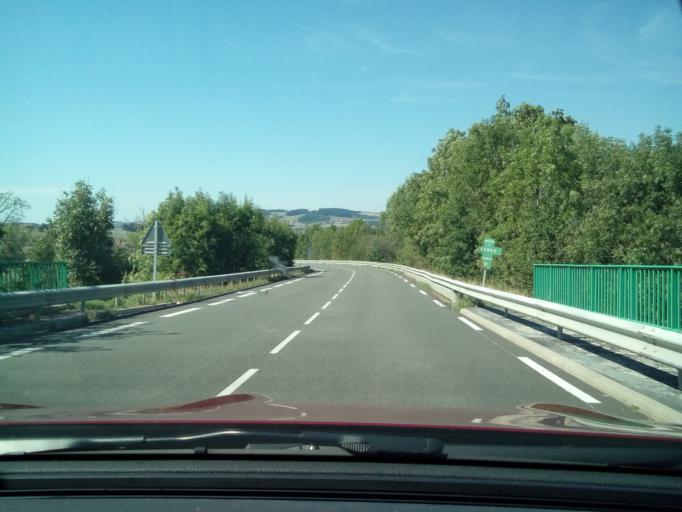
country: FR
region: Rhone-Alpes
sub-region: Departement du Rhone
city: Cublize
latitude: 45.9789
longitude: 4.3839
